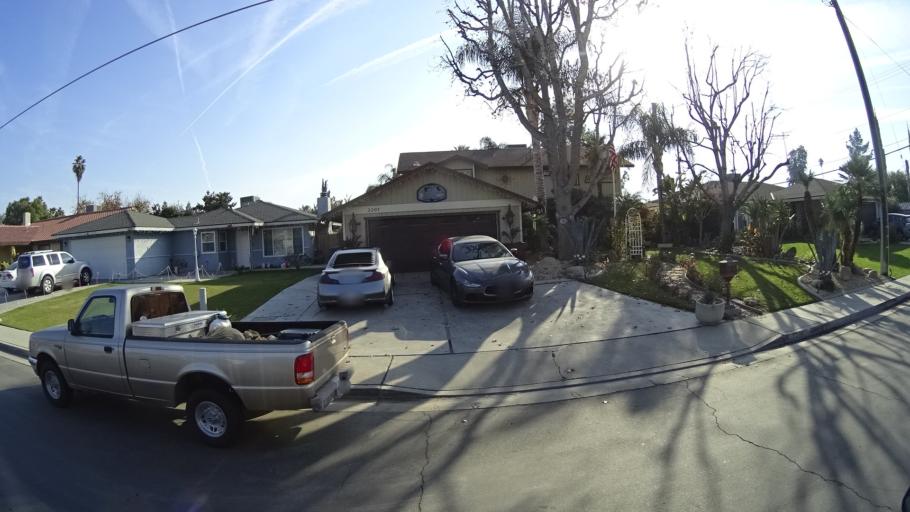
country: US
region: California
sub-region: Kern County
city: Bakersfield
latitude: 35.3235
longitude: -119.0275
